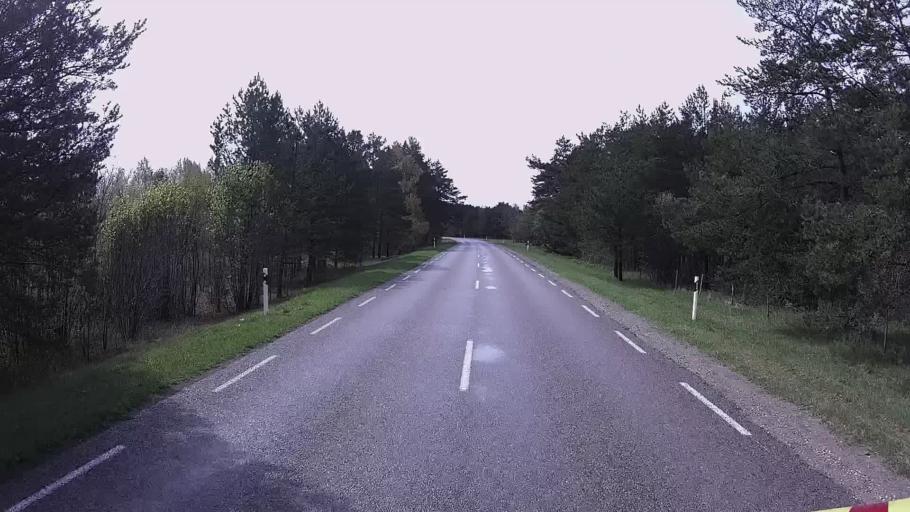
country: EE
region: Hiiumaa
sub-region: Kaerdla linn
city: Kardla
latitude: 58.7241
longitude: 22.6193
